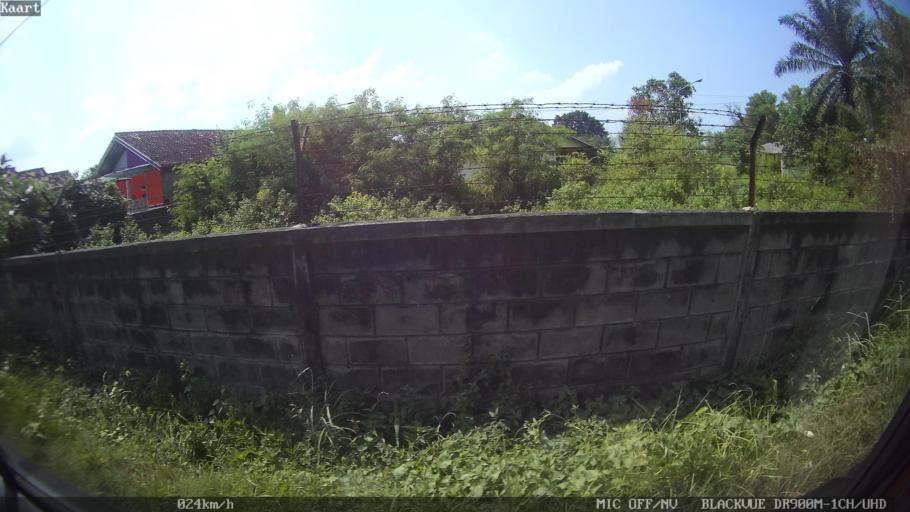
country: ID
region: Lampung
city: Natar
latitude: -5.2665
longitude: 105.1873
